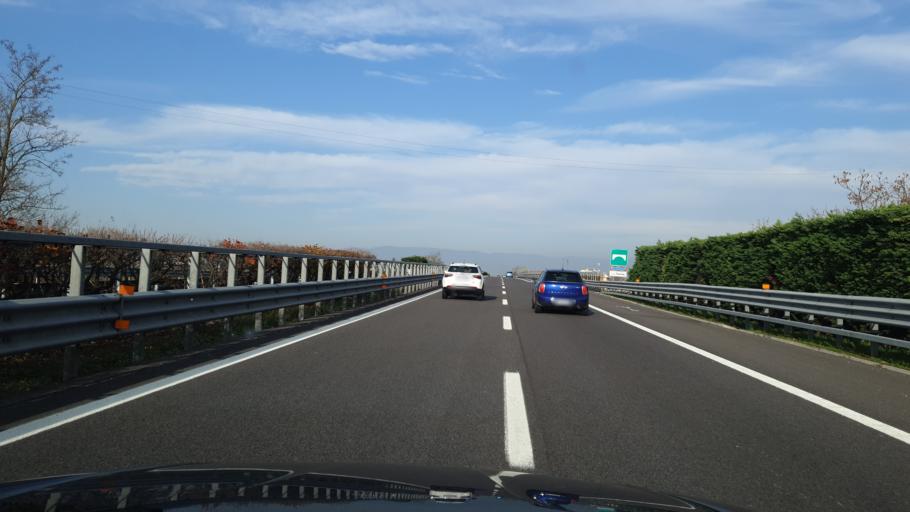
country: IT
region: Veneto
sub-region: Provincia di Vicenza
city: Marola
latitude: 45.5371
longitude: 11.6255
